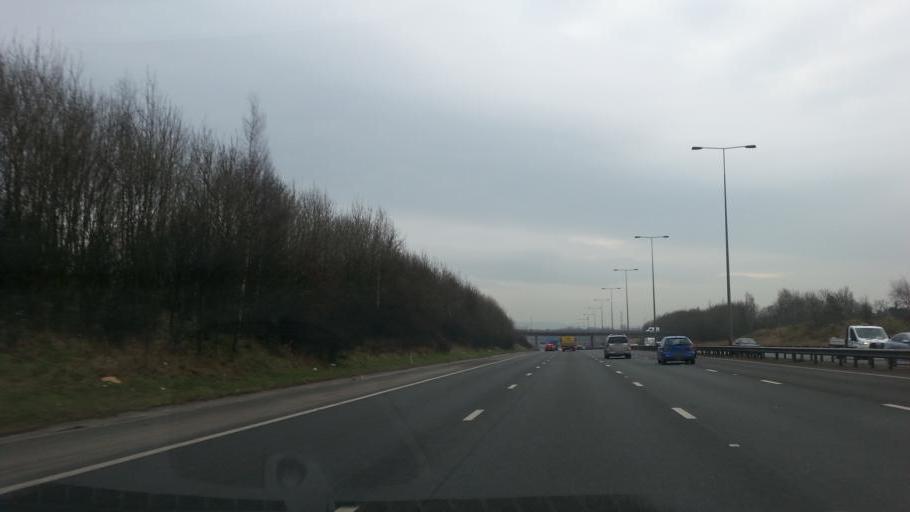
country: GB
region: England
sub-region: Borough of Tameside
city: Droylsden
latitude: 53.5086
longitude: -2.1331
